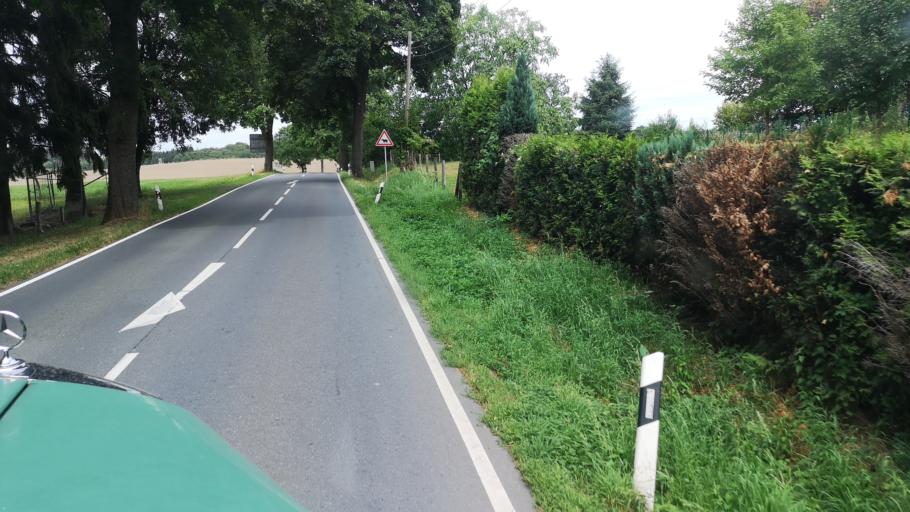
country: DE
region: North Rhine-Westphalia
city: Wermelskirchen
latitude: 51.1109
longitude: 7.2311
